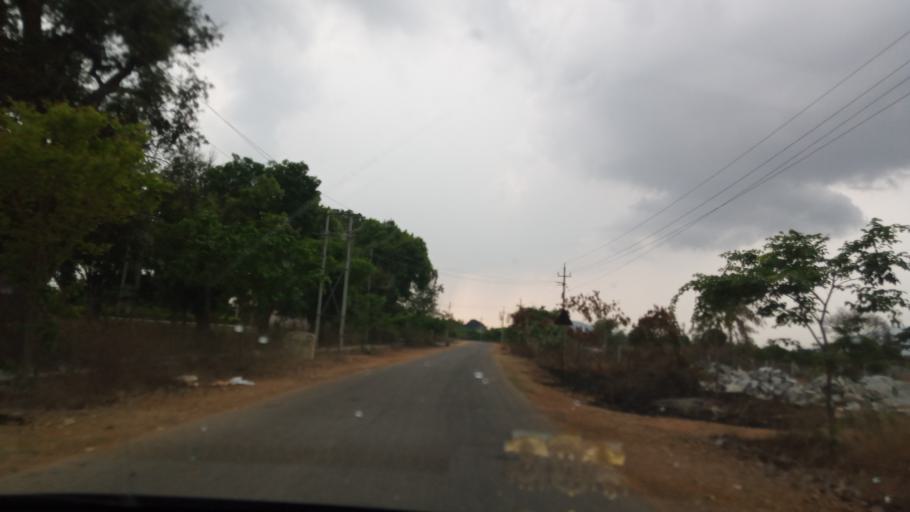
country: IN
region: Karnataka
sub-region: Kolar
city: Mulbagal
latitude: 13.1404
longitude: 78.3642
